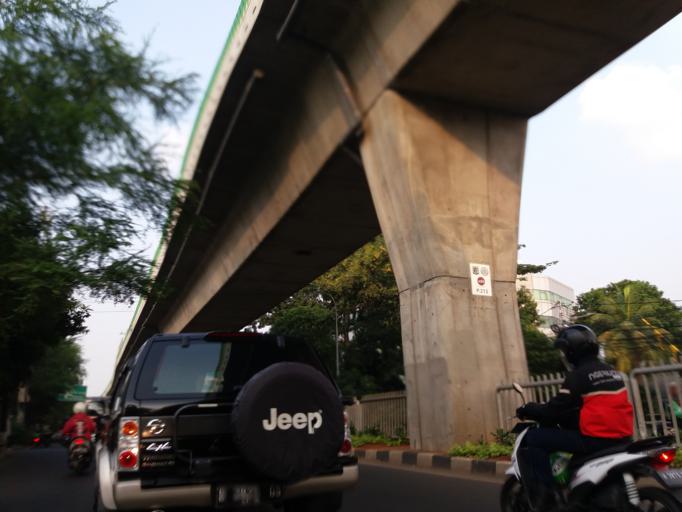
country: ID
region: Jakarta Raya
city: Jakarta
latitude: -6.2405
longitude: 106.8209
